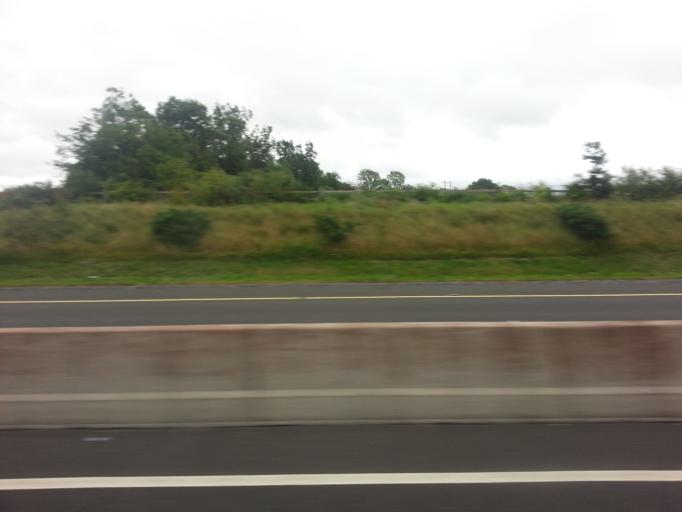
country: IE
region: Leinster
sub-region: County Carlow
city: Bagenalstown
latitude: 52.6976
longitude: -7.0230
